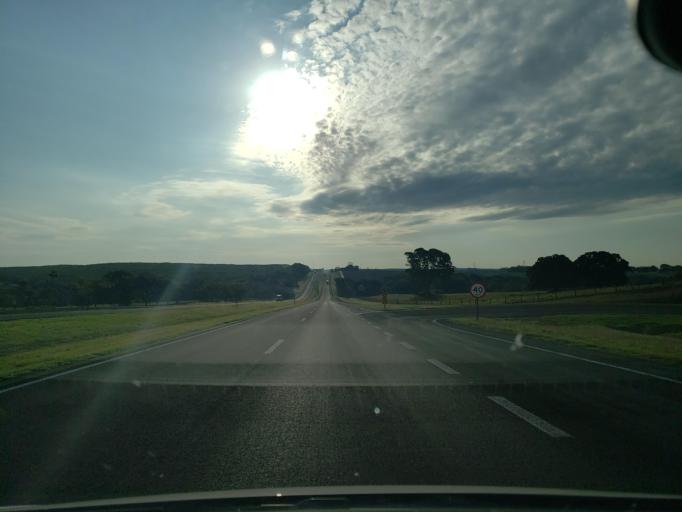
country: BR
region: Sao Paulo
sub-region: Valparaiso
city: Valparaiso
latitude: -21.1896
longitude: -50.9098
